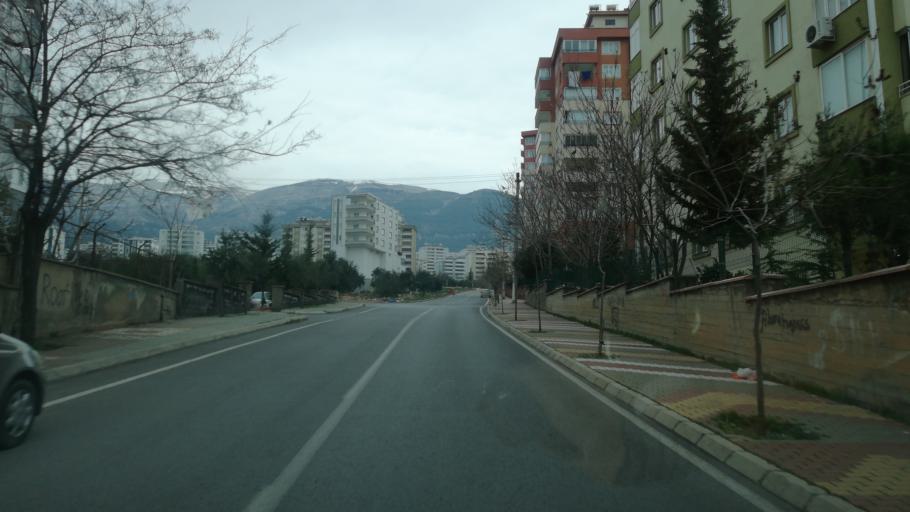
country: TR
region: Kahramanmaras
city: Kahramanmaras
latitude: 37.5926
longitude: 36.8933
